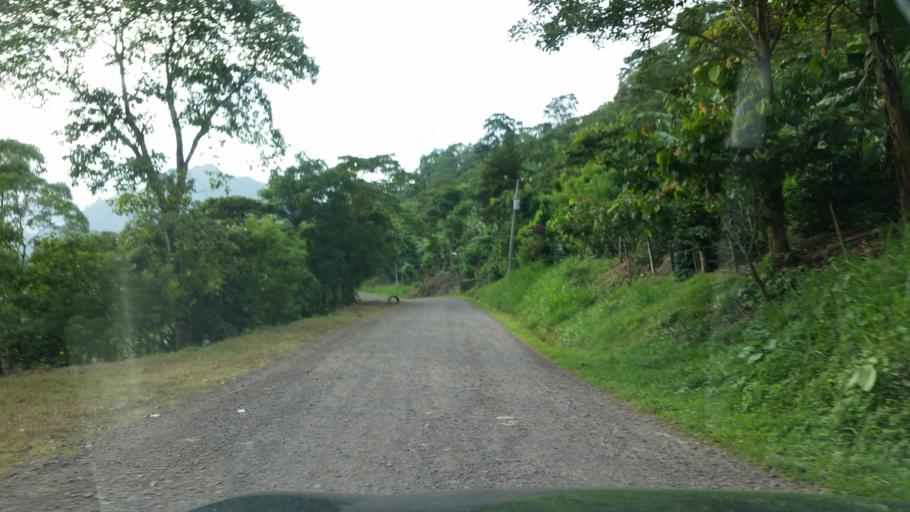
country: NI
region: Jinotega
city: Jinotega
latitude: 13.2419
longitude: -85.7276
